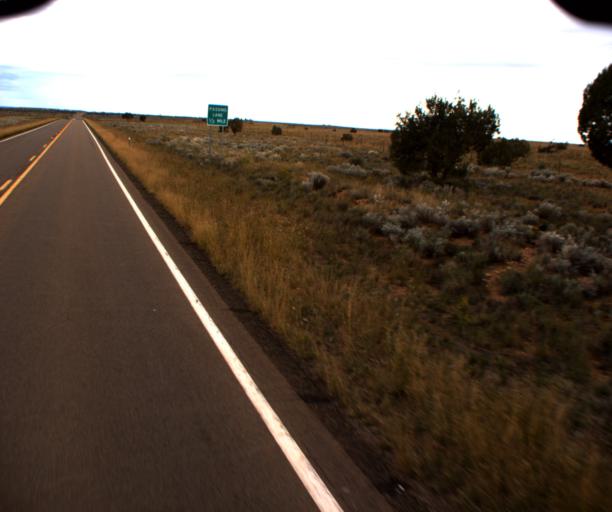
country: US
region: Arizona
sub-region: Navajo County
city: Snowflake
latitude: 34.6022
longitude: -110.0886
